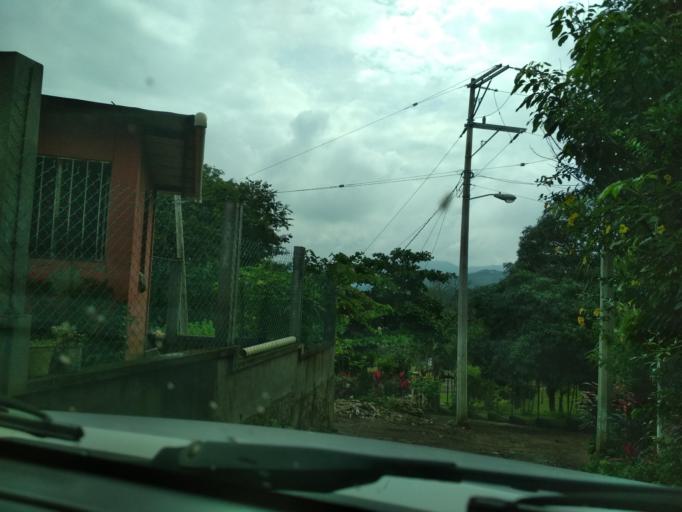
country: MX
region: Veracruz
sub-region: San Andres Tuxtla
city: Cerro las Iguanas
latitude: 18.4103
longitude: -95.1962
